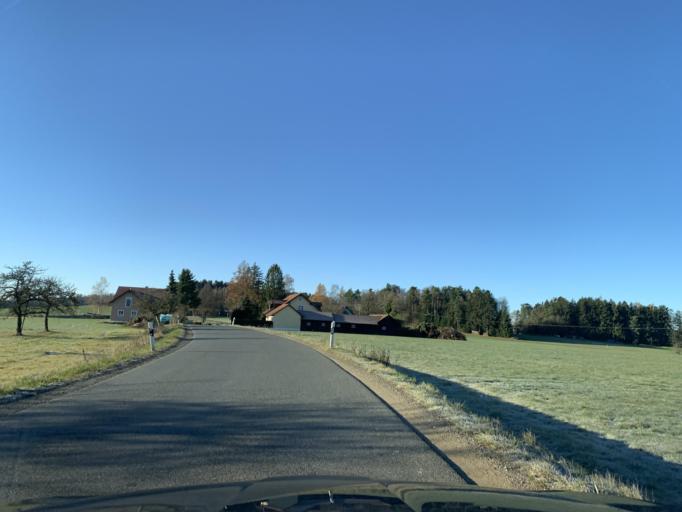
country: DE
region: Bavaria
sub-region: Upper Palatinate
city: Oberviechtach
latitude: 49.4534
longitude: 12.4440
